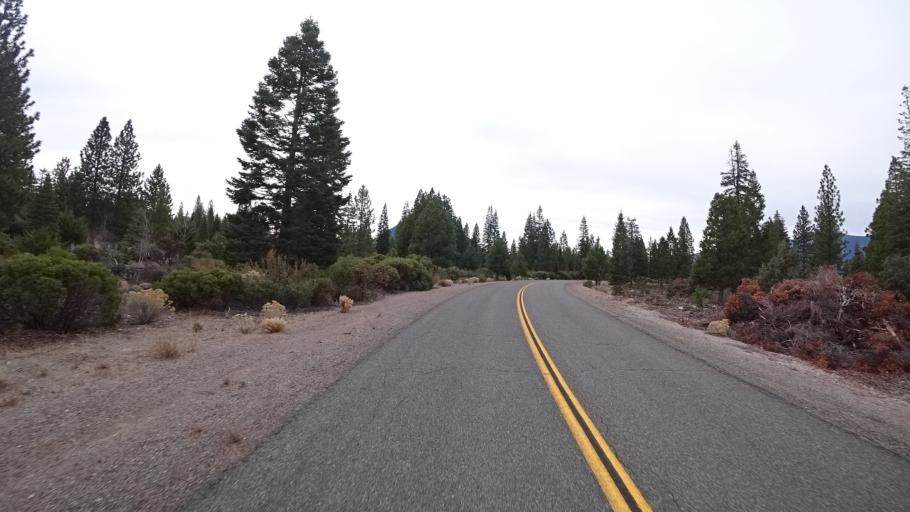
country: US
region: California
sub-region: Siskiyou County
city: Weed
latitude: 41.4097
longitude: -122.3646
